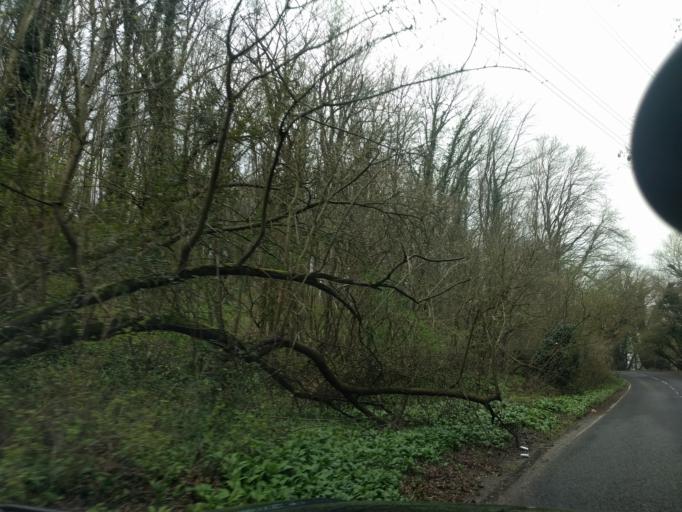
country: GB
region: England
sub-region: Wiltshire
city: Box
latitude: 51.3995
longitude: -2.2860
